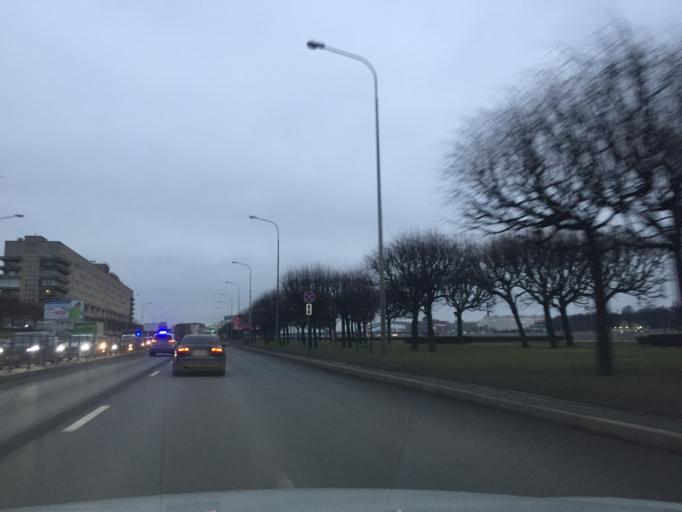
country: RU
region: Leningrad
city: Finlyandskiy
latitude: 59.9526
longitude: 30.4074
